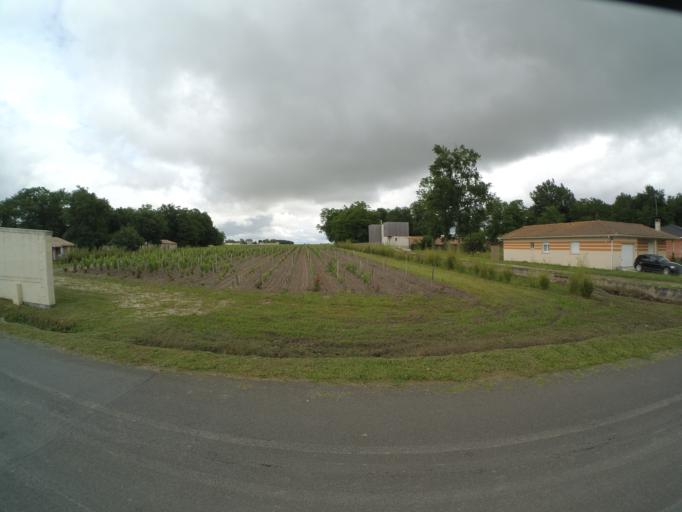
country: FR
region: Aquitaine
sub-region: Departement de la Gironde
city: Lamarque
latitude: 45.0891
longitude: -0.7255
